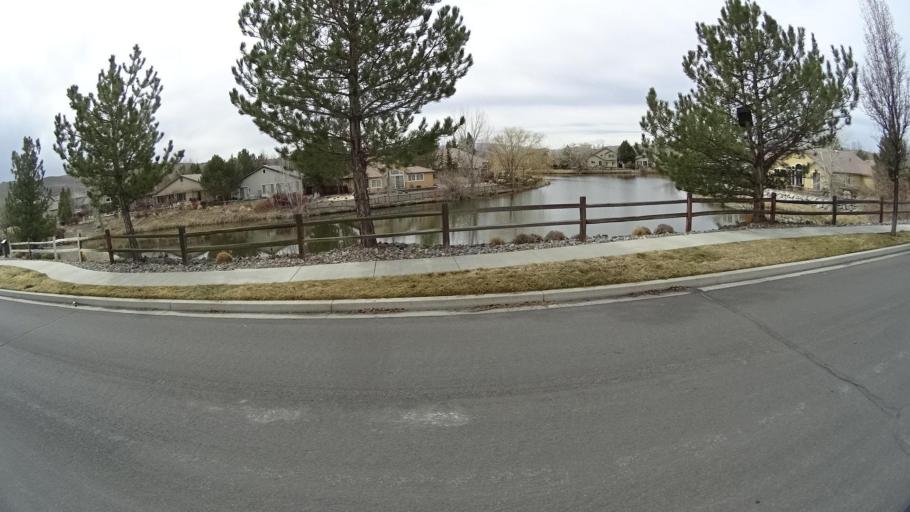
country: US
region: Nevada
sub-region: Washoe County
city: Spanish Springs
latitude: 39.6127
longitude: -119.6903
